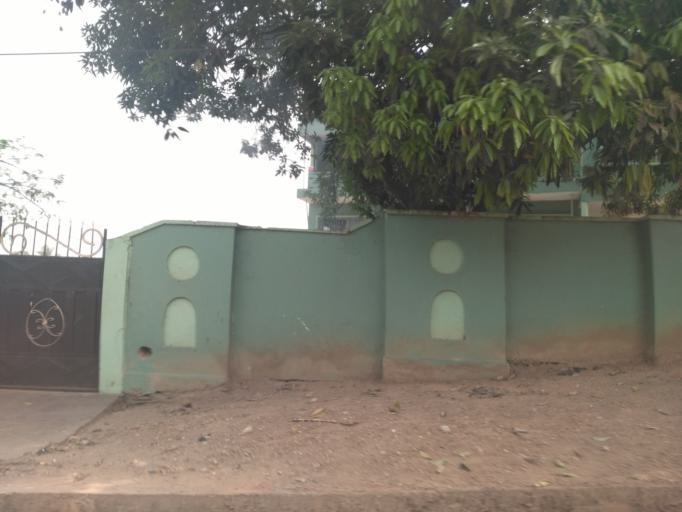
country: GH
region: Ashanti
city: Kumasi
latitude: 6.6792
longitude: -1.5980
